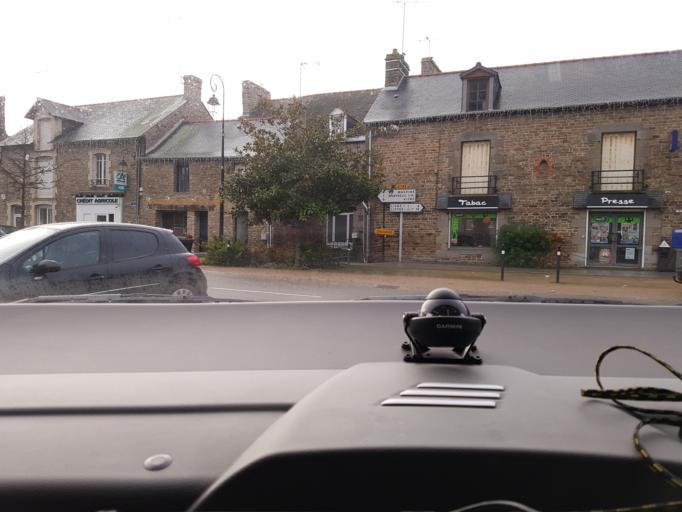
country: FR
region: Brittany
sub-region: Departement d'Ille-et-Vilaine
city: Livre-sur-Changeon
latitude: 48.1769
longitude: -1.3024
